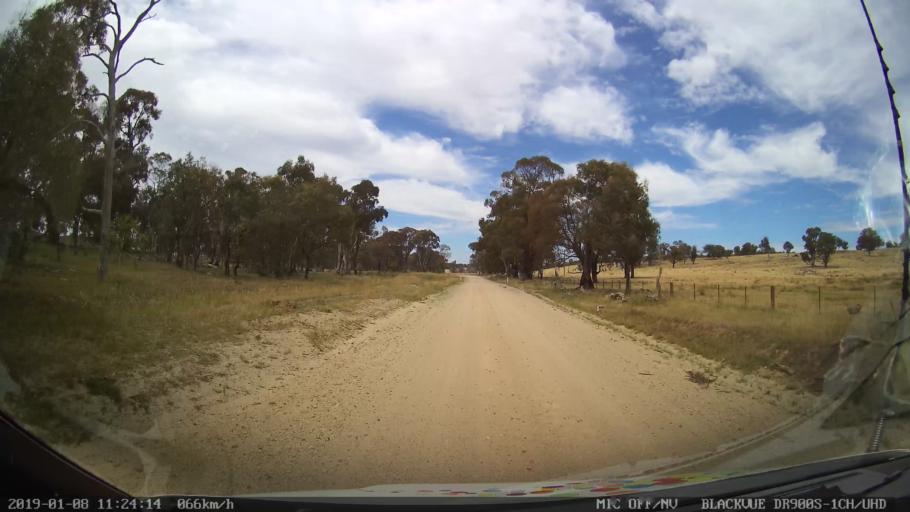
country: AU
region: New South Wales
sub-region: Guyra
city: Guyra
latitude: -30.2627
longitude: 151.5582
